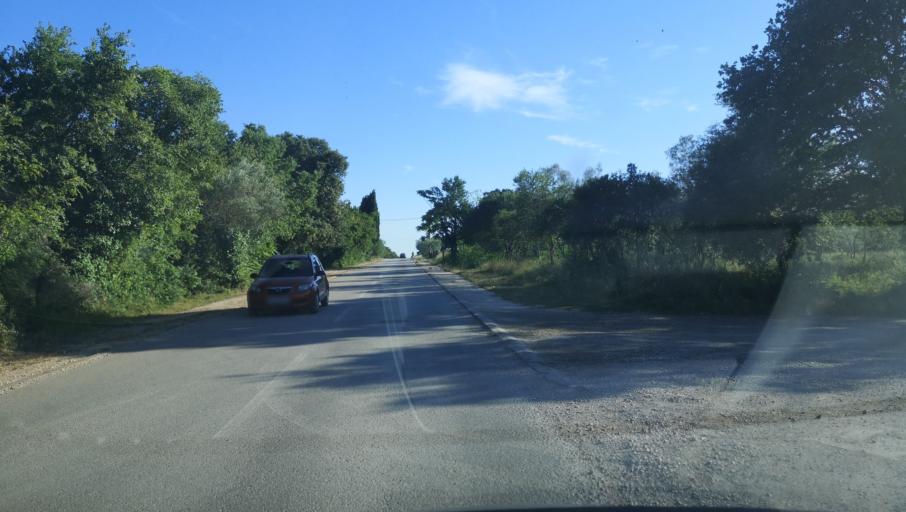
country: HR
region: Istarska
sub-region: Grad Rovinj
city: Rovinj
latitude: 45.0611
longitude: 13.6899
